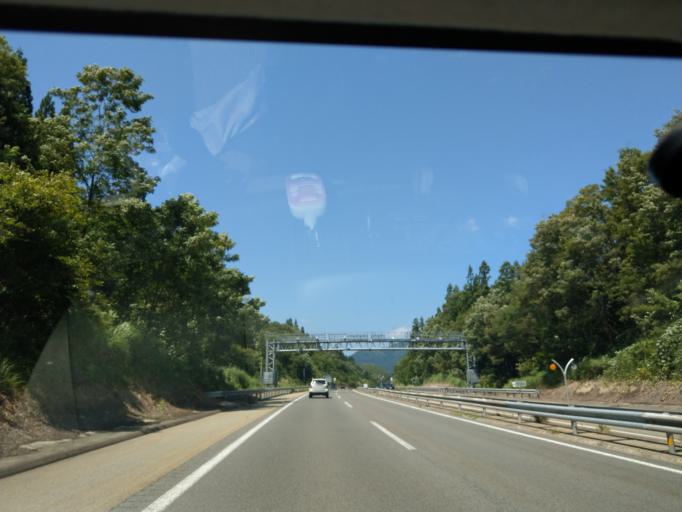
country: JP
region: Akita
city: Omagari
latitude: 39.4127
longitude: 140.4395
